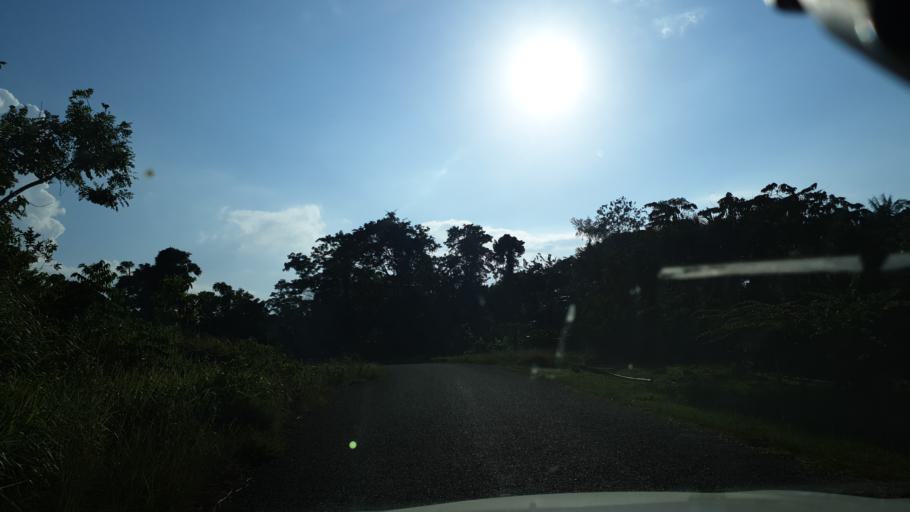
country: PG
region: East Sepik
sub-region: Wewak
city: Wewak
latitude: -3.6928
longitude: 143.6532
